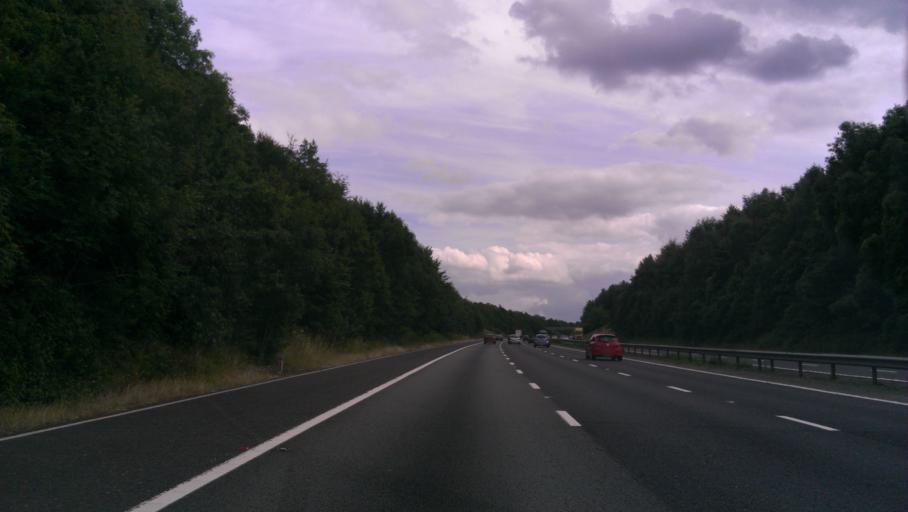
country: GB
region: England
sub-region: Kent
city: Longfield
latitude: 51.3572
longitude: 0.2713
